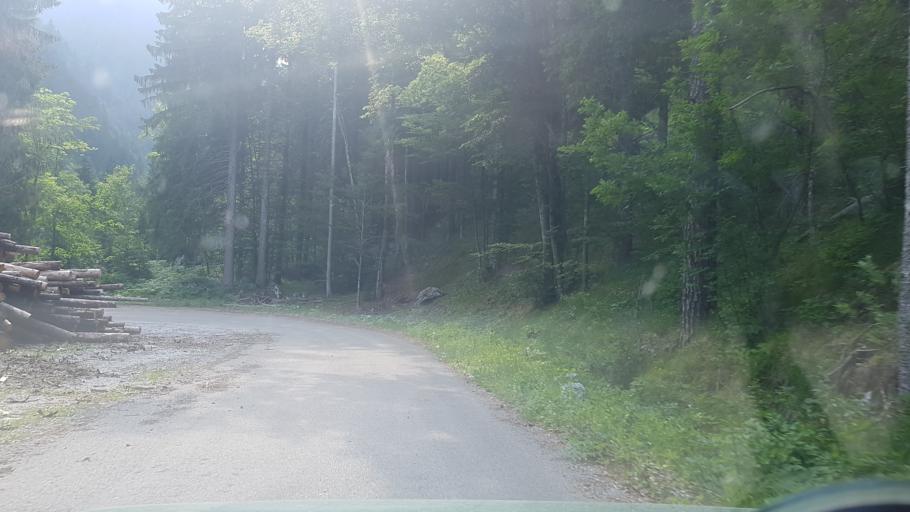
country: IT
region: Friuli Venezia Giulia
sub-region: Provincia di Udine
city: Pontebba
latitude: 46.5262
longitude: 13.2248
